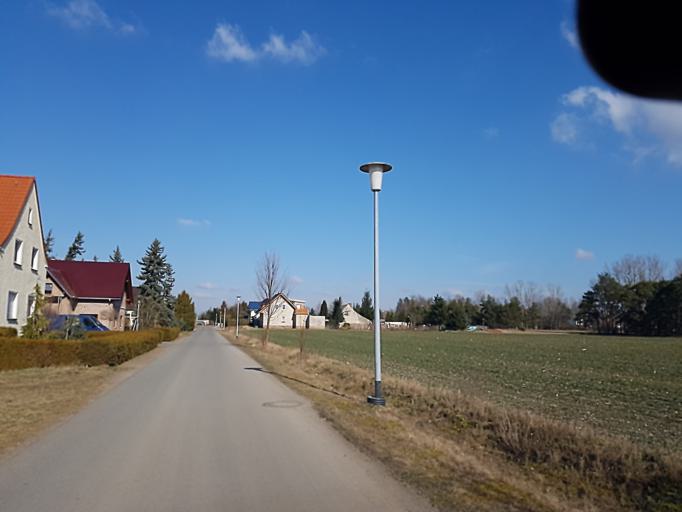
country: DE
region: Brandenburg
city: Ruckersdorf
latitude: 51.5893
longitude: 13.5438
